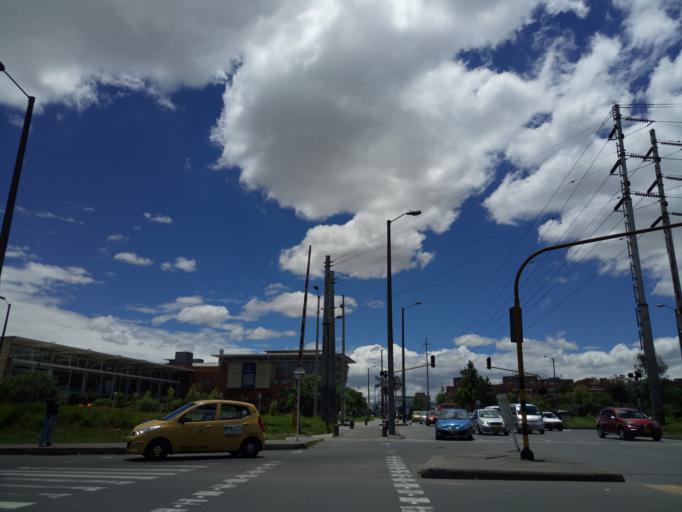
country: CO
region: Bogota D.C.
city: Bogota
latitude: 4.6660
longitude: -74.1302
